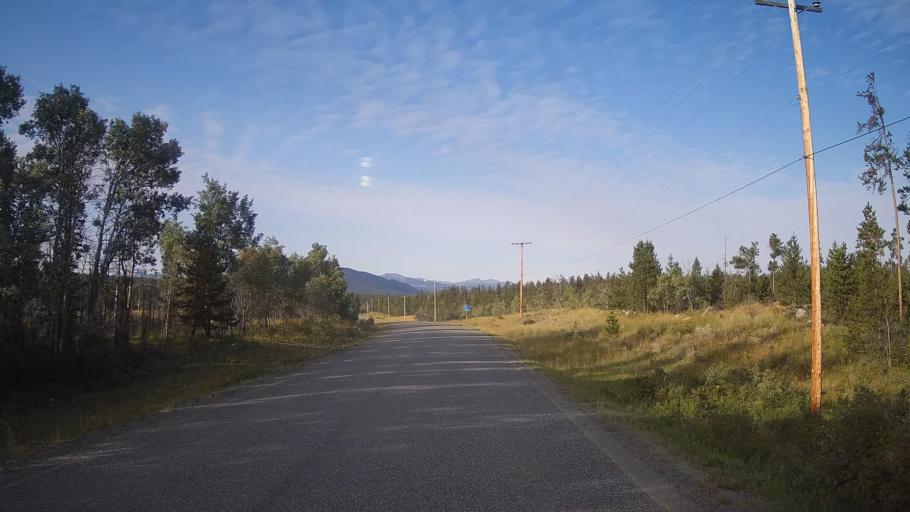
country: CA
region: British Columbia
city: Hanceville
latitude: 51.9464
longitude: -124.4576
